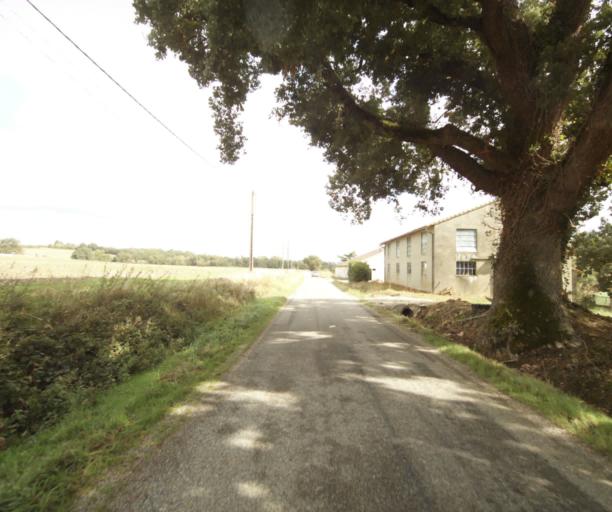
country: FR
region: Midi-Pyrenees
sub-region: Departement du Tarn-et-Garonne
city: Finhan
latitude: 43.8716
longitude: 1.1225
